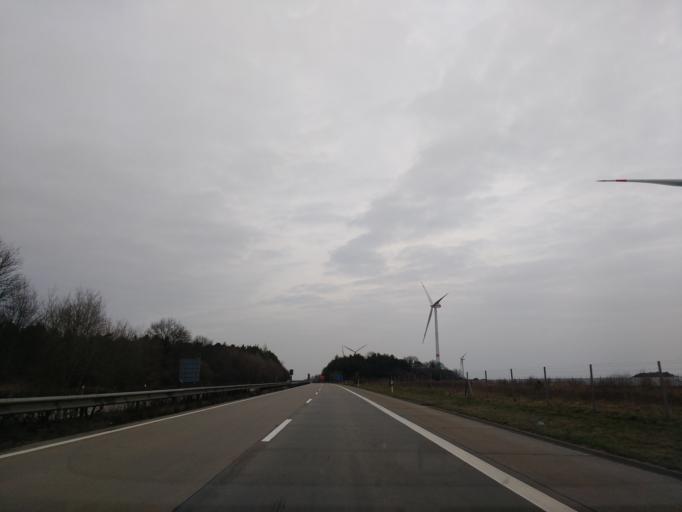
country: DE
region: Lower Saxony
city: Langen
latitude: 53.6255
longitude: 8.6654
